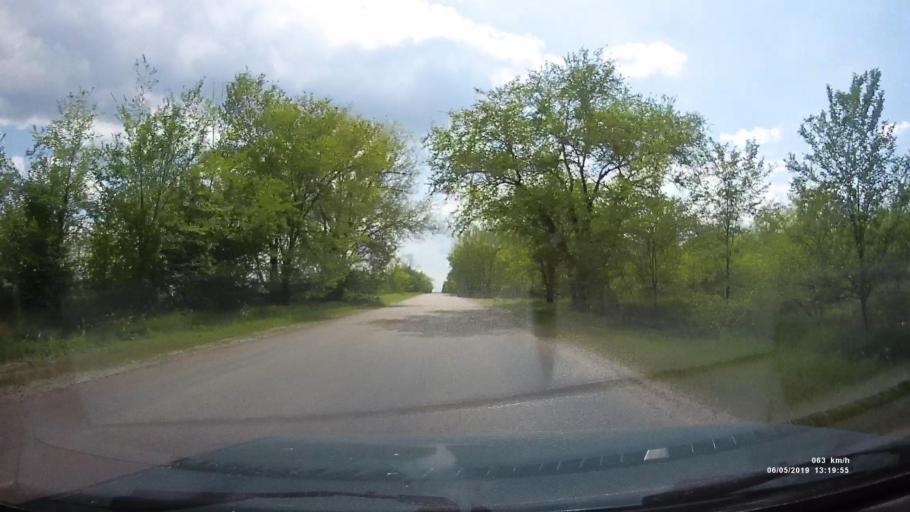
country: RU
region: Rostov
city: Ust'-Donetskiy
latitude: 47.7212
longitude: 40.9123
